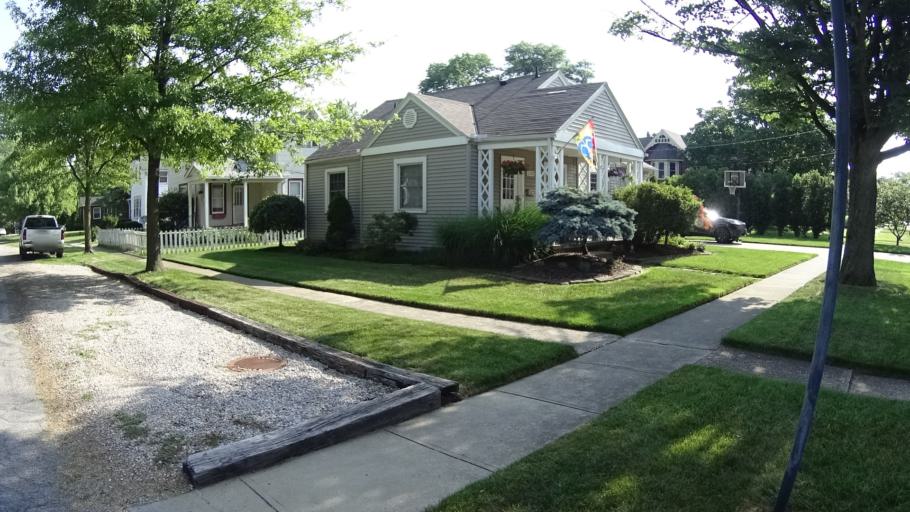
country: US
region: Ohio
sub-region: Lorain County
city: Vermilion
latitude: 41.4191
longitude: -82.3601
